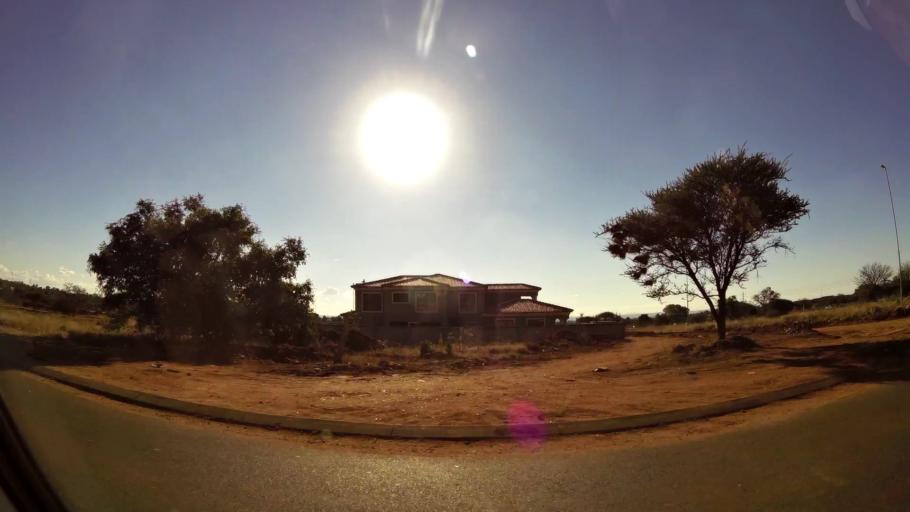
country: ZA
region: Limpopo
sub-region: Capricorn District Municipality
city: Polokwane
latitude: -23.8831
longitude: 29.4969
